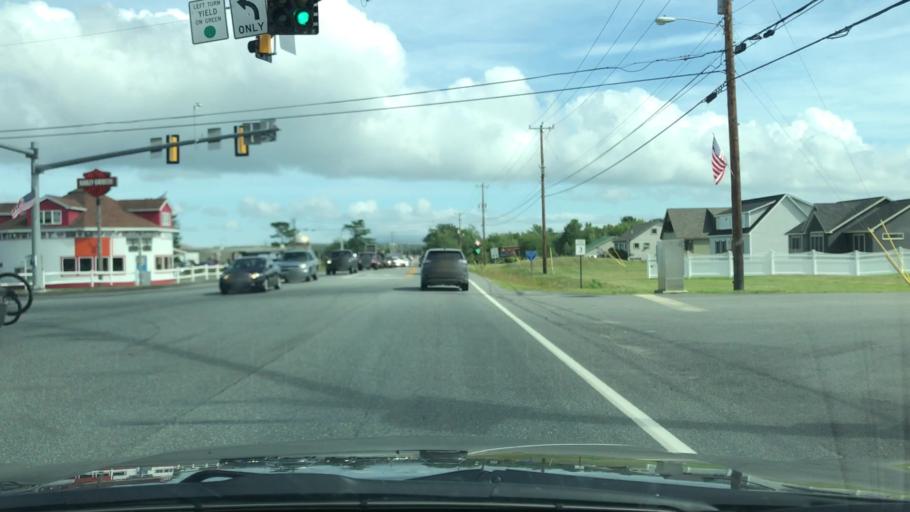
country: US
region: Maine
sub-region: Hancock County
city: Trenton
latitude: 44.4886
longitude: -68.3711
